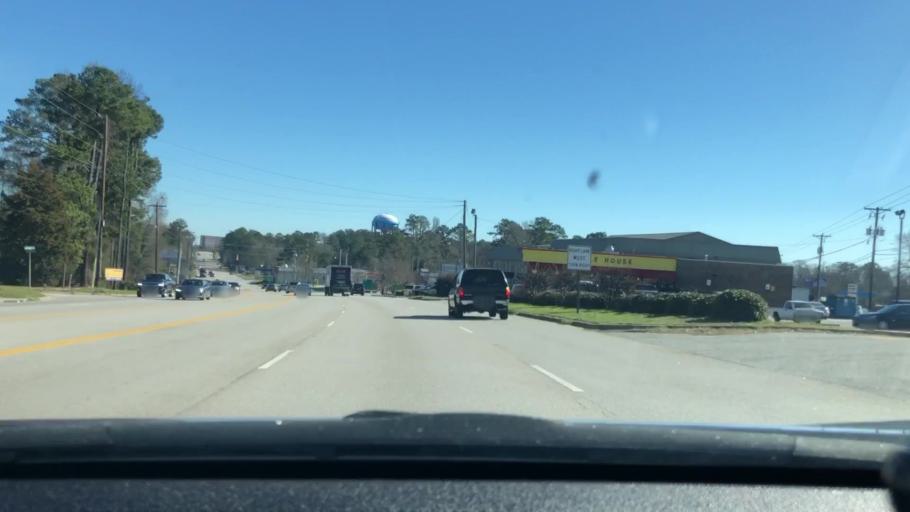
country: US
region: South Carolina
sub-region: Lexington County
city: Oak Grove
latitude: 34.0080
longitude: -81.1438
